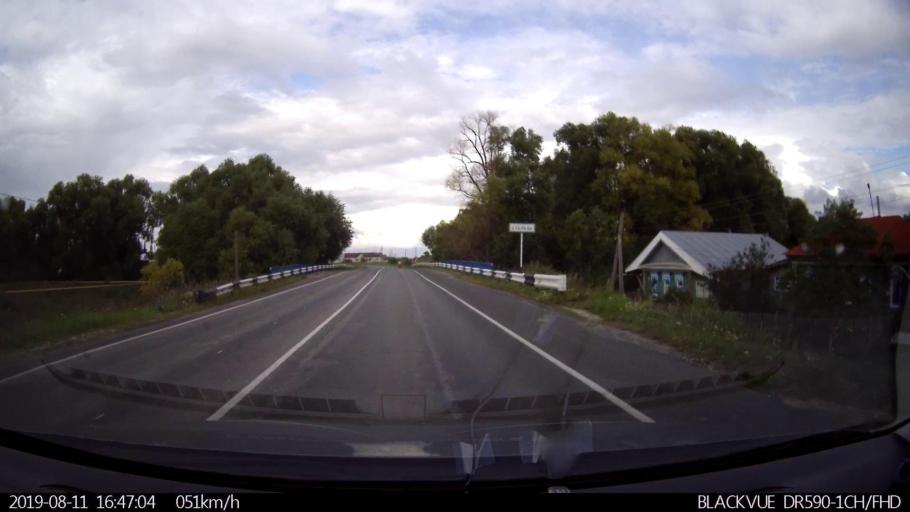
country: RU
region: Ulyanovsk
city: Mayna
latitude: 54.2011
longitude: 47.6942
